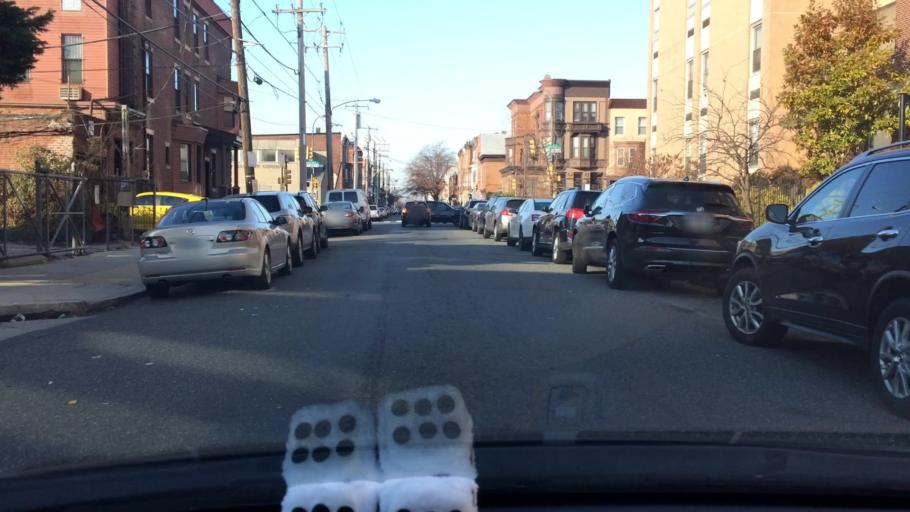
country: US
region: Pennsylvania
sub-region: Philadelphia County
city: Philadelphia
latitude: 39.9206
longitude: -75.1698
